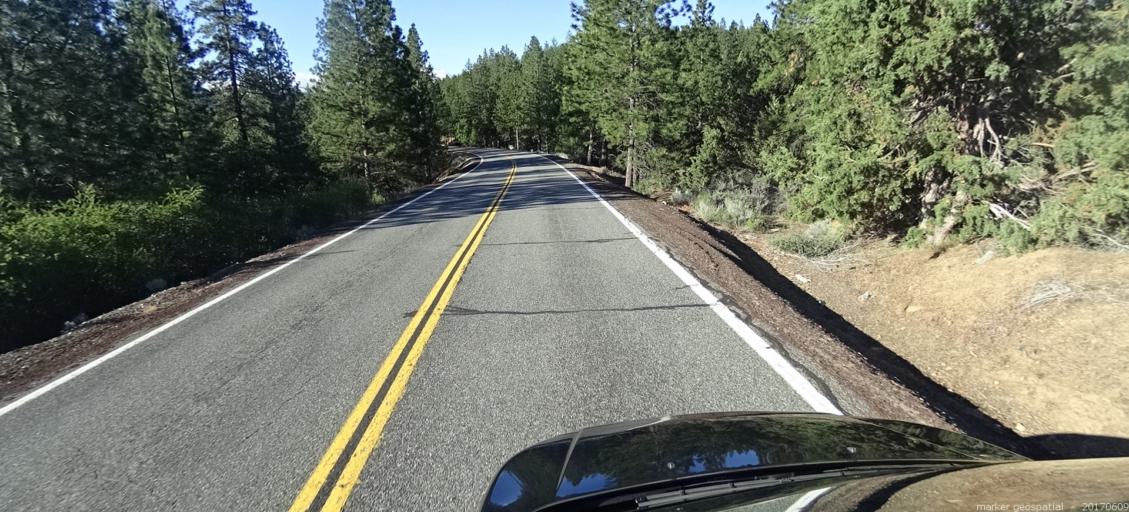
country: US
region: California
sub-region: Siskiyou County
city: Weed
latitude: 41.4271
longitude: -122.6369
